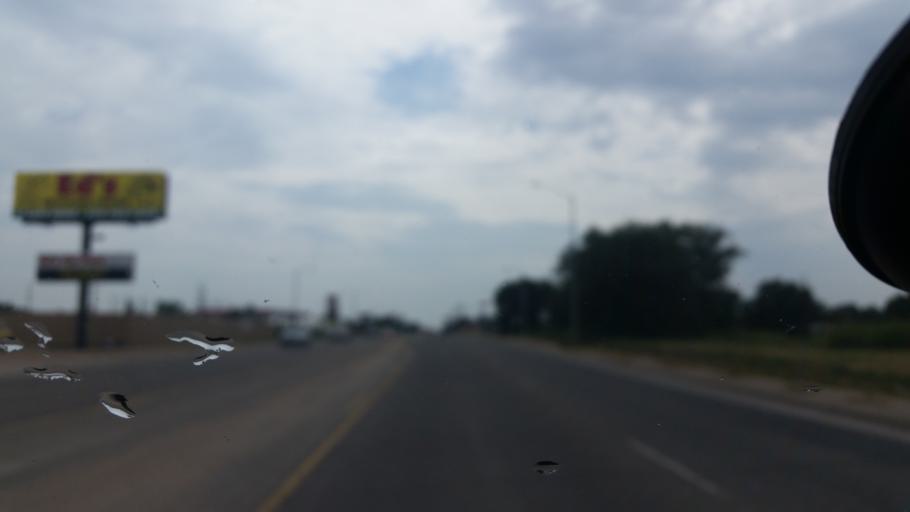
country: US
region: New Mexico
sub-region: Curry County
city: Clovis
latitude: 34.3923
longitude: -103.1965
